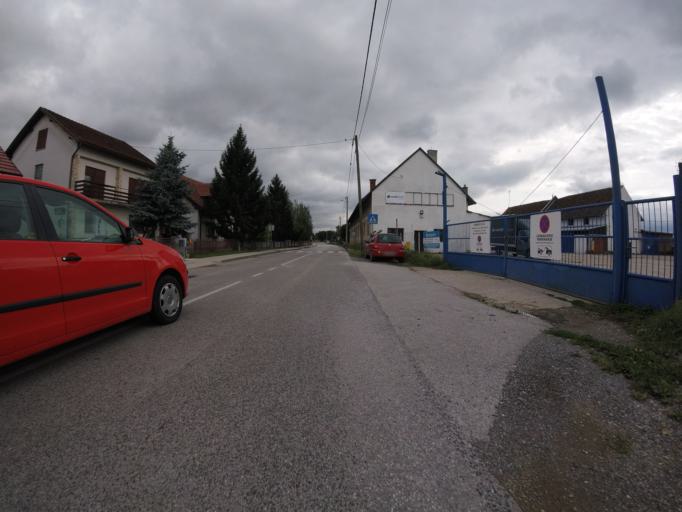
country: HR
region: Zagrebacka
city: Gradici
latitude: 45.7069
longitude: 16.0403
